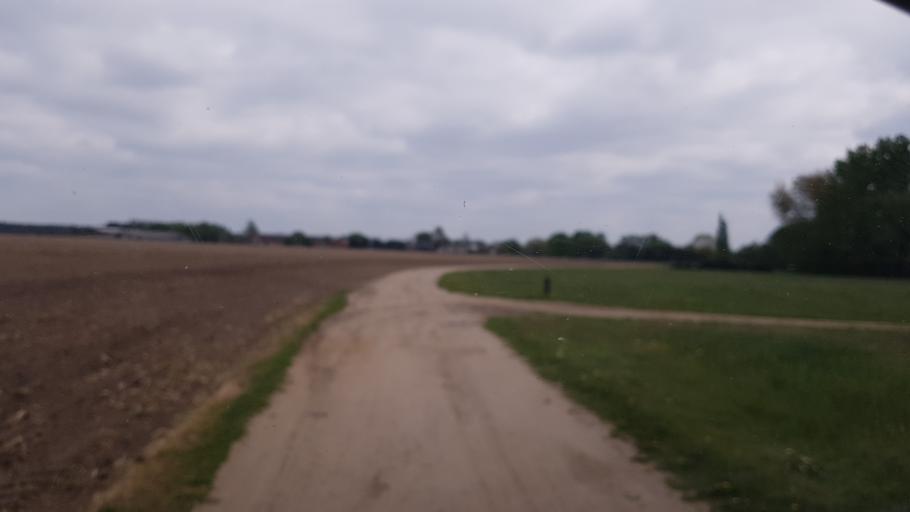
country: DE
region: Brandenburg
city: Schonewalde
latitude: 51.6681
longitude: 13.6203
